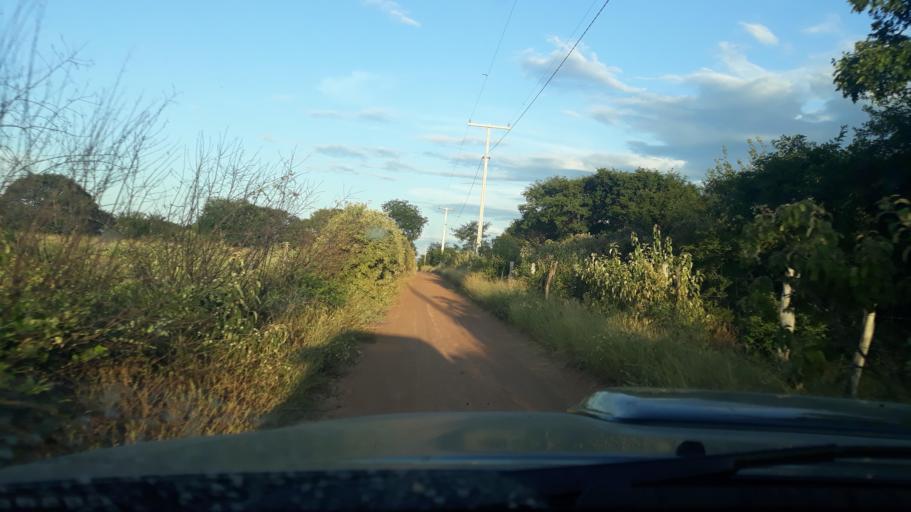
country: BR
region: Bahia
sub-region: Riacho De Santana
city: Riacho de Santana
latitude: -13.8617
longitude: -43.0288
